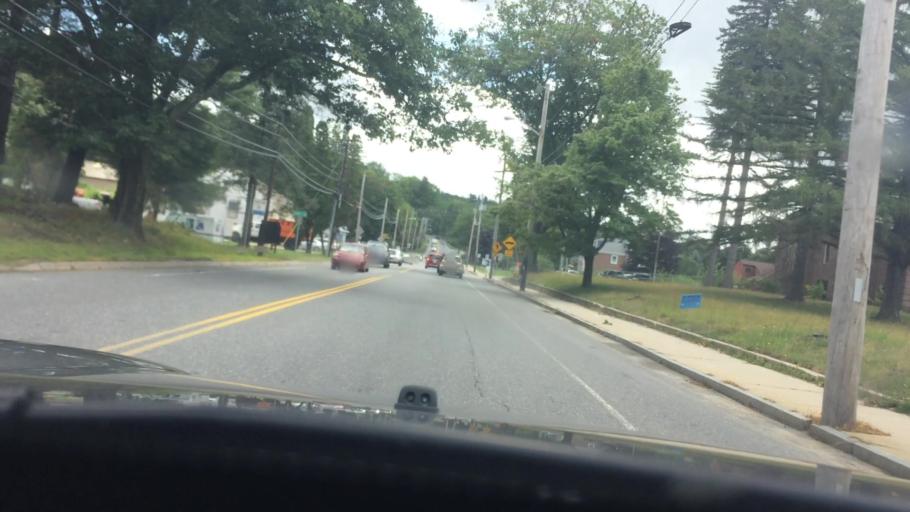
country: US
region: Massachusetts
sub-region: Worcester County
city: Athol
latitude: 42.5850
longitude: -72.2062
